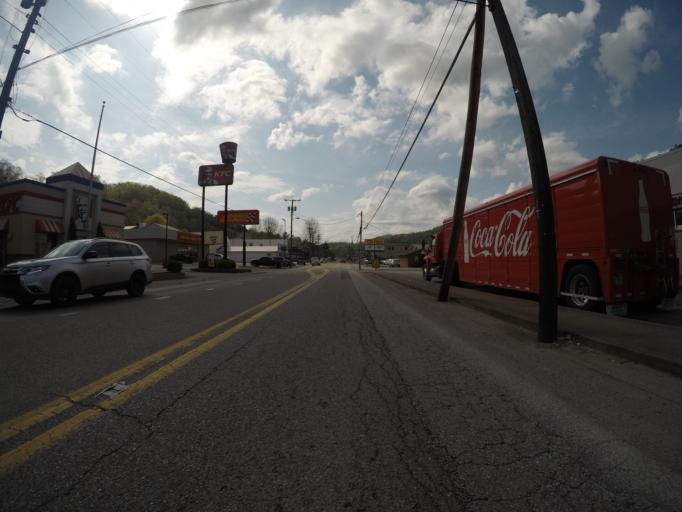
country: US
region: West Virginia
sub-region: Boone County
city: Madison
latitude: 38.0805
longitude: -81.8339
